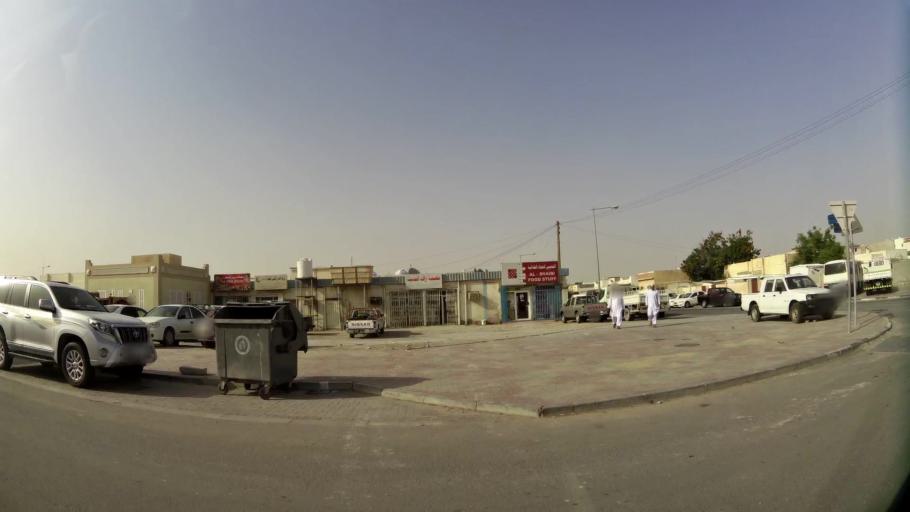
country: QA
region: Baladiyat ar Rayyan
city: Ar Rayyan
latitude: 25.2336
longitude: 51.4358
